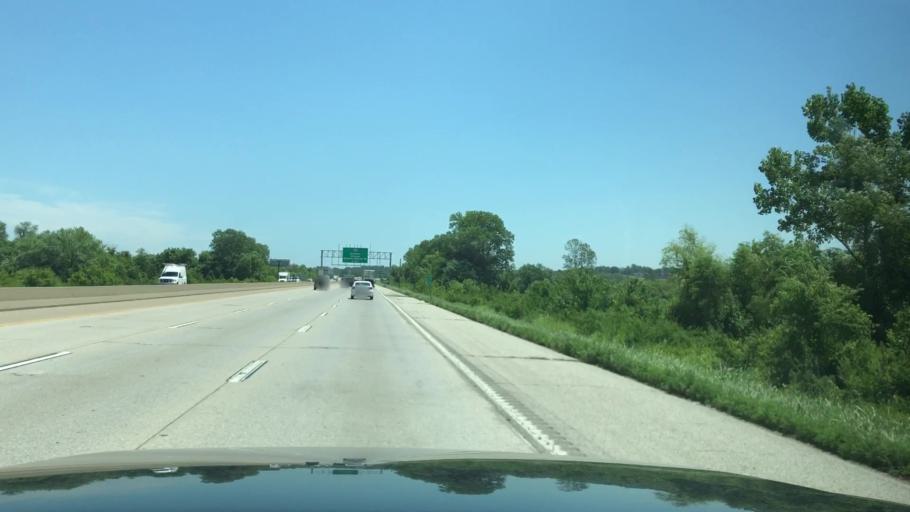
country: US
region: Missouri
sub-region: Saint Louis County
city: Bridgeton
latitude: 38.7908
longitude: -90.4360
